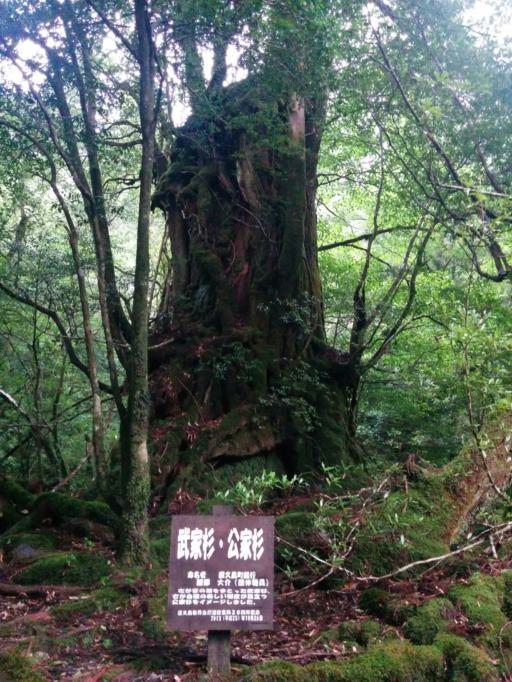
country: JP
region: Kagoshima
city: Nishinoomote
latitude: 30.3661
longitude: 130.5685
